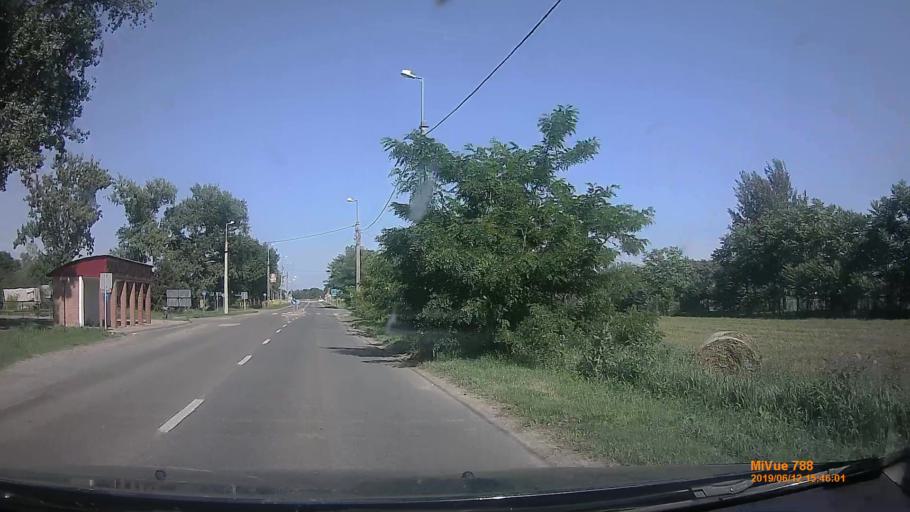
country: HU
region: Csongrad
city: Mako
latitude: 46.2168
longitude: 20.5168
